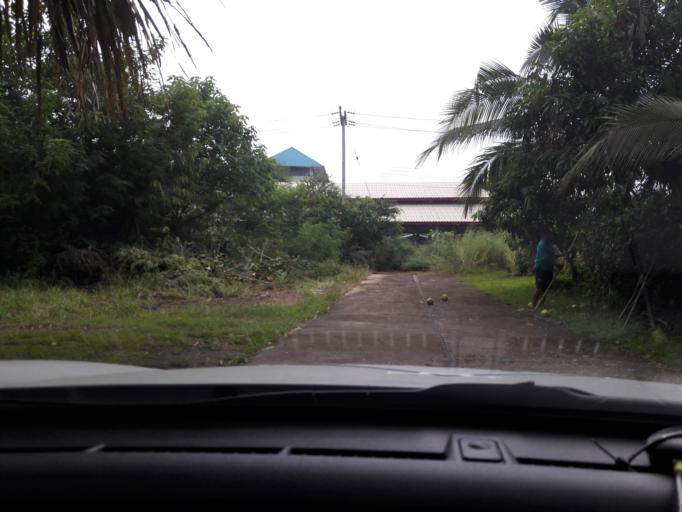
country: TH
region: Nakhon Sawan
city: Tak Fa
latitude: 15.3528
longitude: 100.4937
